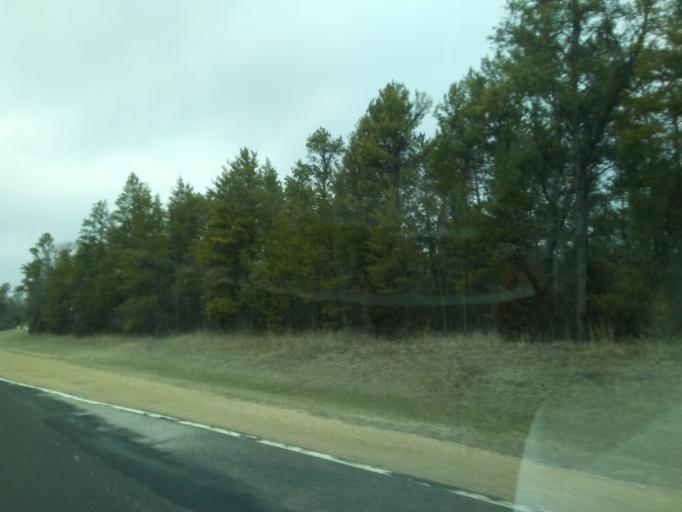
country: US
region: Wisconsin
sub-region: Richland County
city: Richland Center
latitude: 43.2161
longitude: -90.2845
